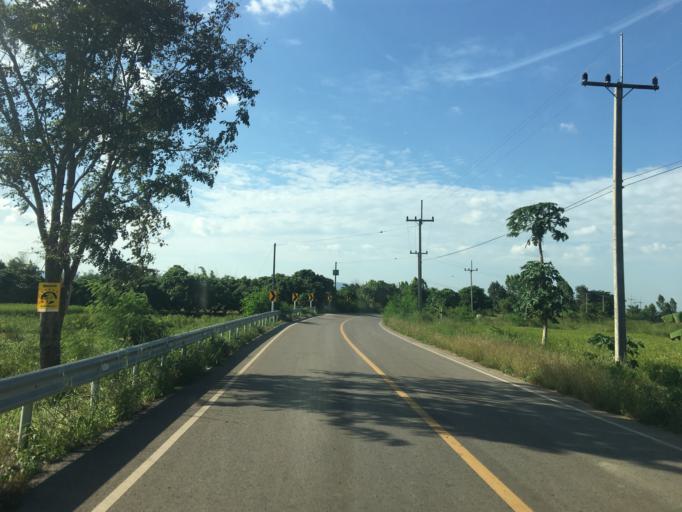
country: TH
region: Chiang Rai
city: Pa Daet
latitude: 19.4332
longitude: 100.0109
